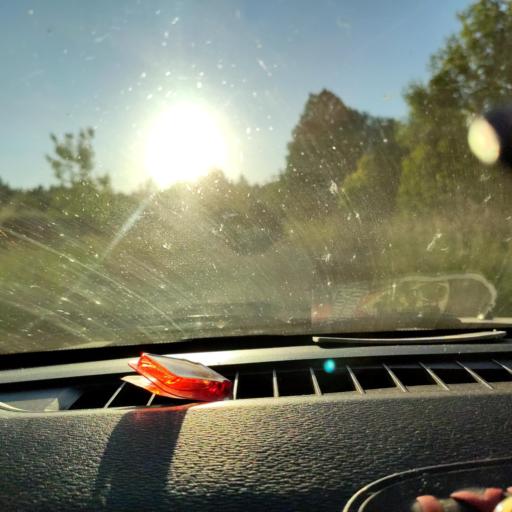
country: RU
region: Perm
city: Froly
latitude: 57.9447
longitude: 56.1984
